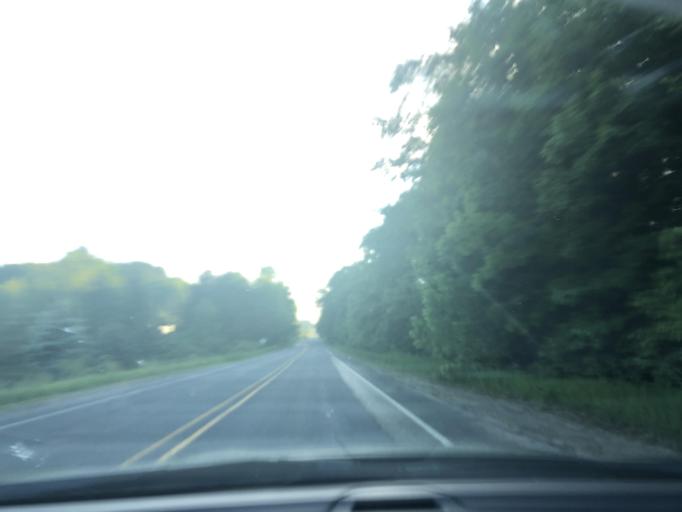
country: US
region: Michigan
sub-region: Missaukee County
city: Lake City
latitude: 44.4664
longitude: -85.0754
